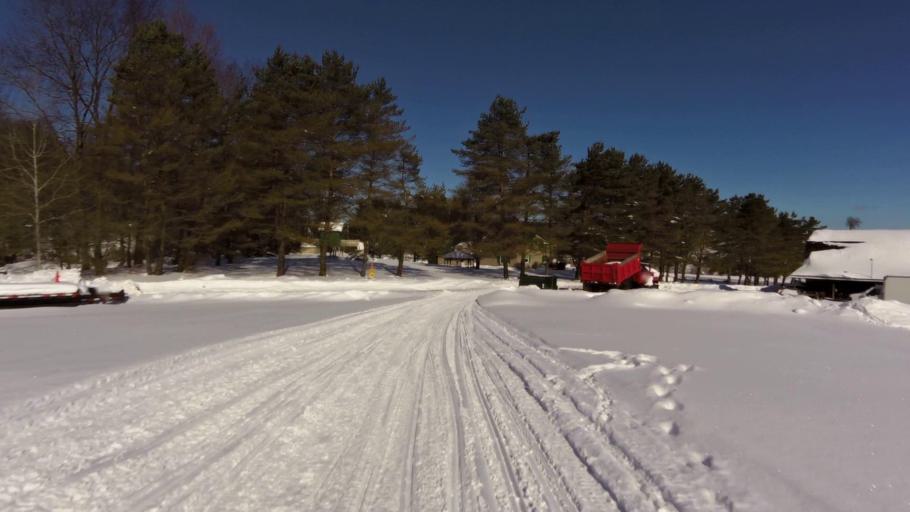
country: US
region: New York
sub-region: Cattaraugus County
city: Franklinville
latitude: 42.4031
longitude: -78.5022
